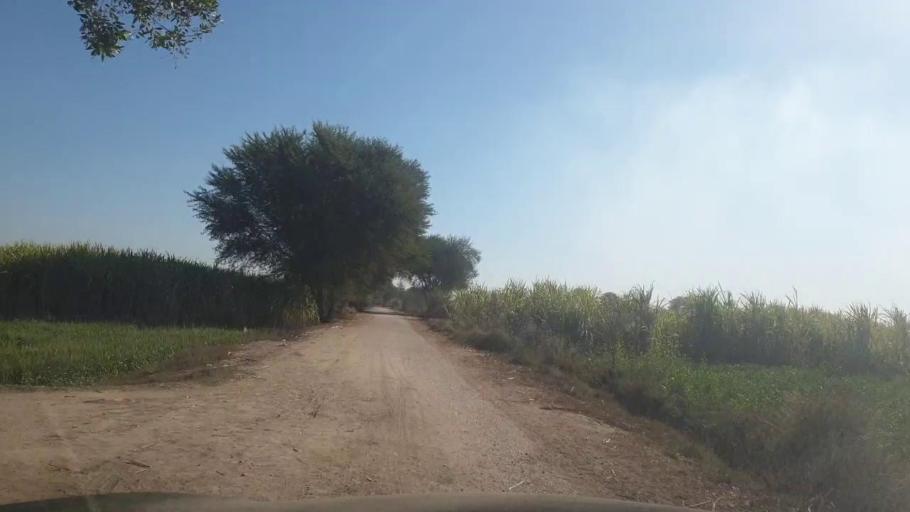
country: PK
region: Sindh
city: Adilpur
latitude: 27.9690
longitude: 69.3335
